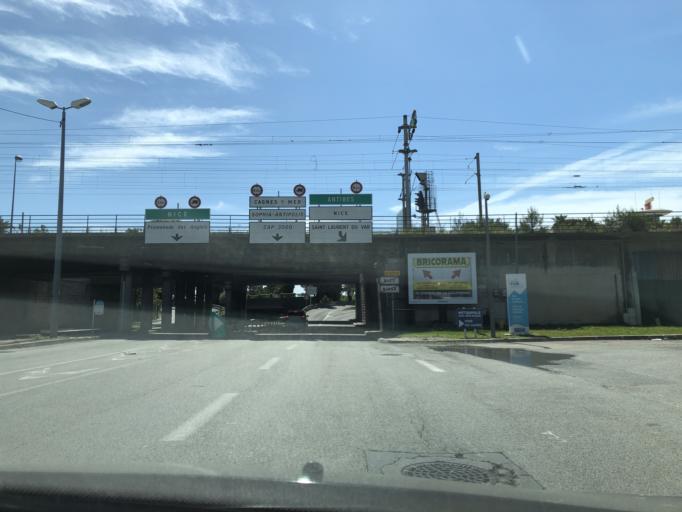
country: FR
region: Provence-Alpes-Cote d'Azur
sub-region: Departement des Alpes-Maritimes
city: Saint-Laurent-du-Var
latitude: 43.6670
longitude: 7.2048
